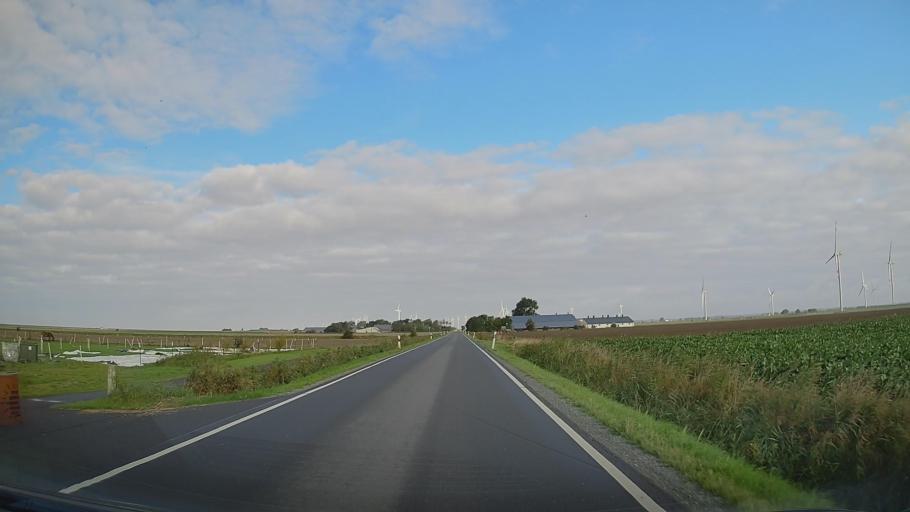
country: DE
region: Schleswig-Holstein
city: Reussenkoge
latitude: 54.5735
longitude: 8.9282
